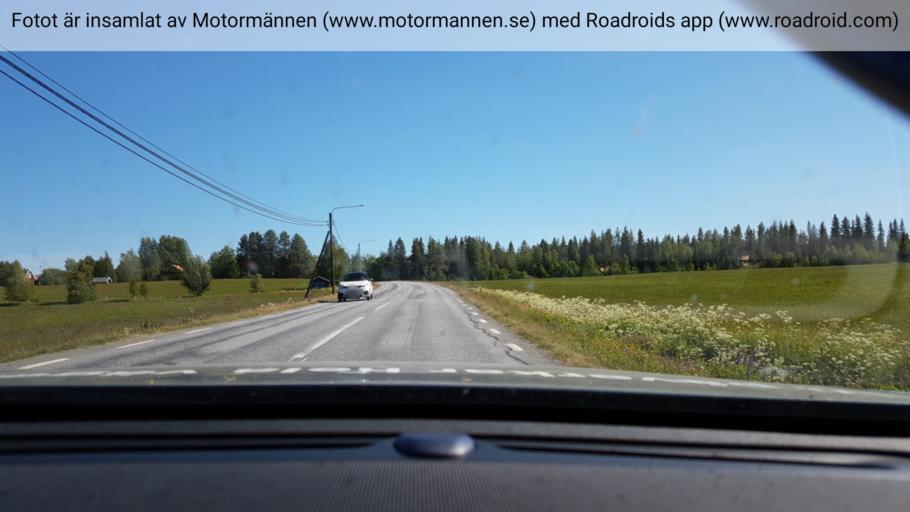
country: SE
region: Vaesterbotten
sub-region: Vilhelmina Kommun
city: Sjoberg
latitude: 64.6421
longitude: 16.3560
